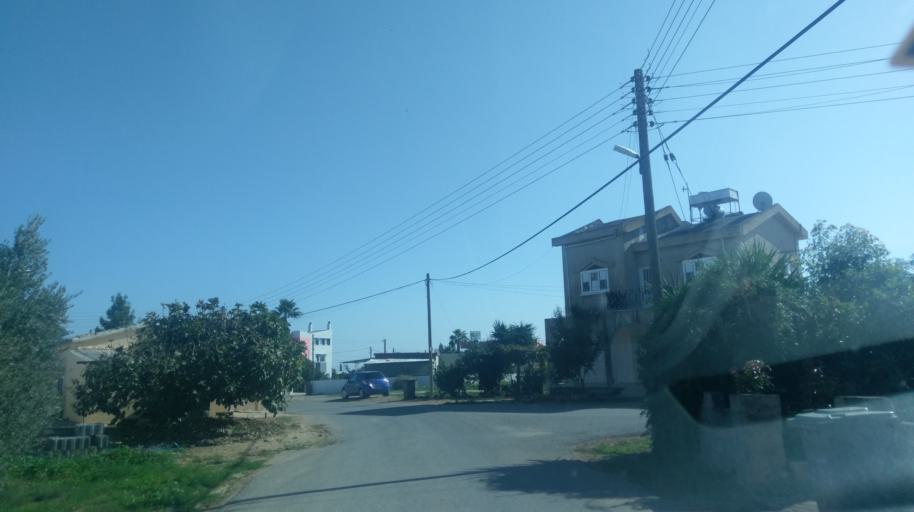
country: CY
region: Ammochostos
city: Trikomo
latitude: 35.2376
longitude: 33.8568
